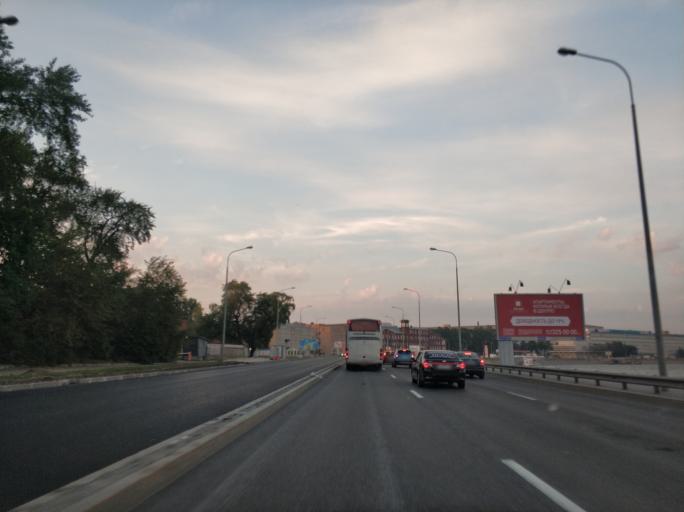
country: RU
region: Leningrad
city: Finlyandskiy
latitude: 59.9574
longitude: 30.3796
